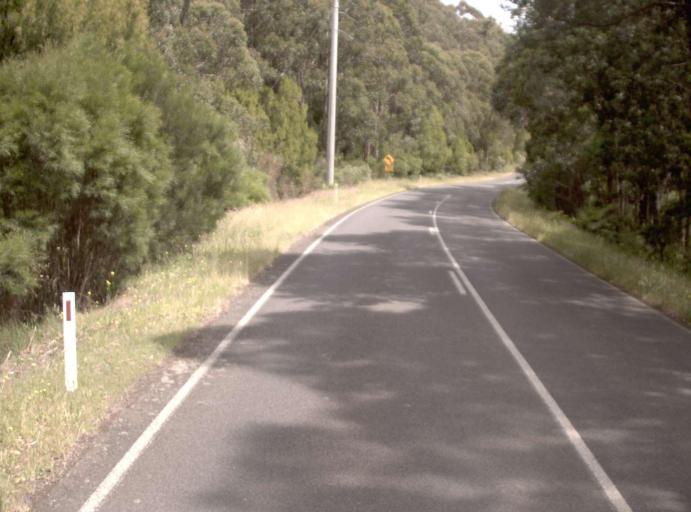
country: AU
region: Victoria
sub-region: Latrobe
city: Moe
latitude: -37.9027
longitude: 146.3900
